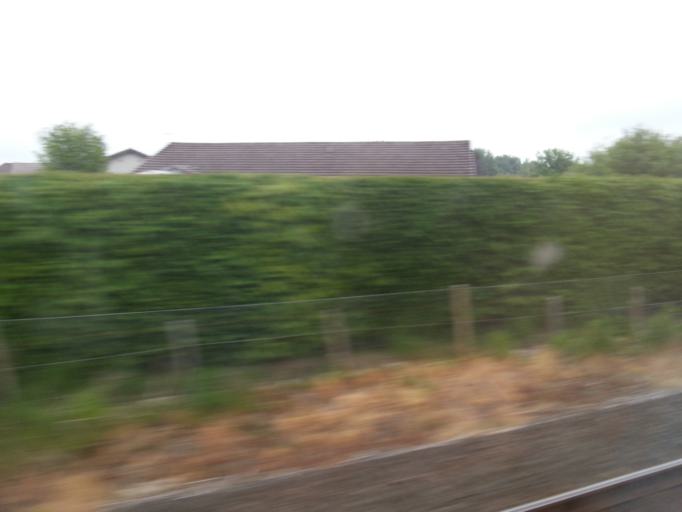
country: GB
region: Scotland
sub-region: Perth and Kinross
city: Luncarty
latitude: 56.4533
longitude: -3.4724
